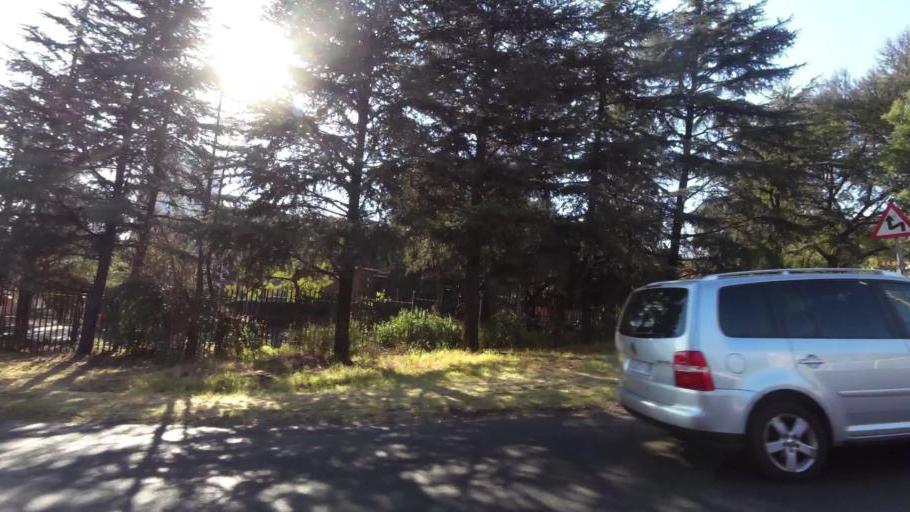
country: ZA
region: Gauteng
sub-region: City of Johannesburg Metropolitan Municipality
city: Johannesburg
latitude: -26.1897
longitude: 28.0077
